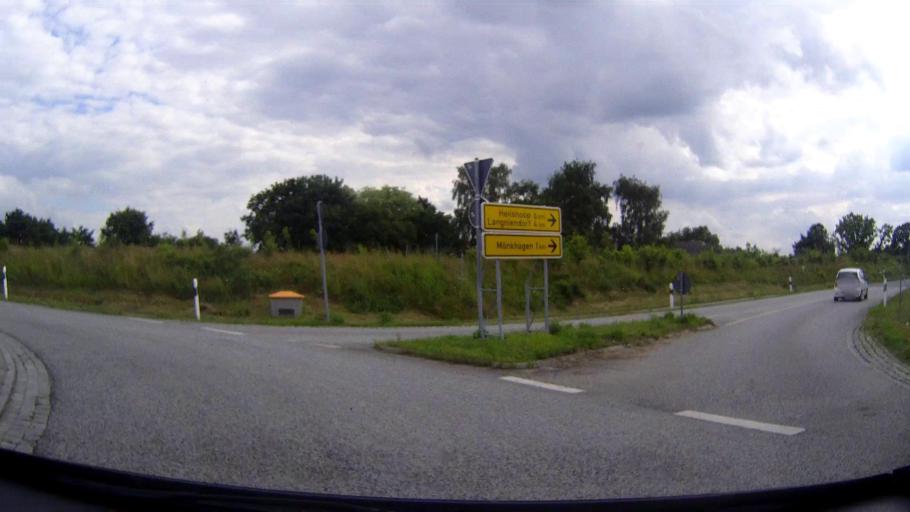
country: DE
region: Schleswig-Holstein
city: Monkhagen
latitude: 53.8997
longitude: 10.5666
